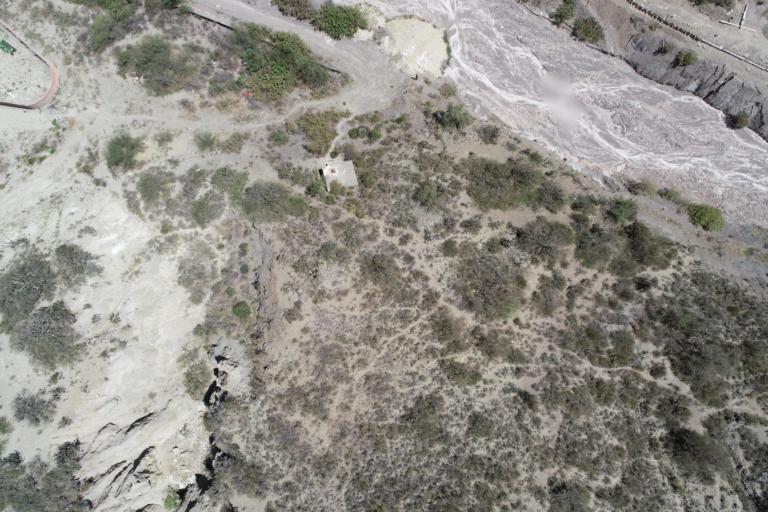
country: BO
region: La Paz
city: La Paz
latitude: -16.6452
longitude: -68.0389
